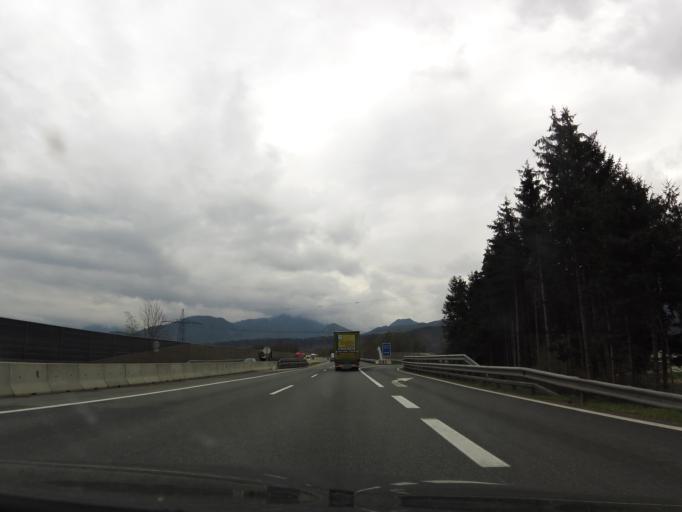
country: AT
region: Tyrol
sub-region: Politischer Bezirk Kufstein
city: Langkampfen
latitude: 47.5326
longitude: 12.0896
